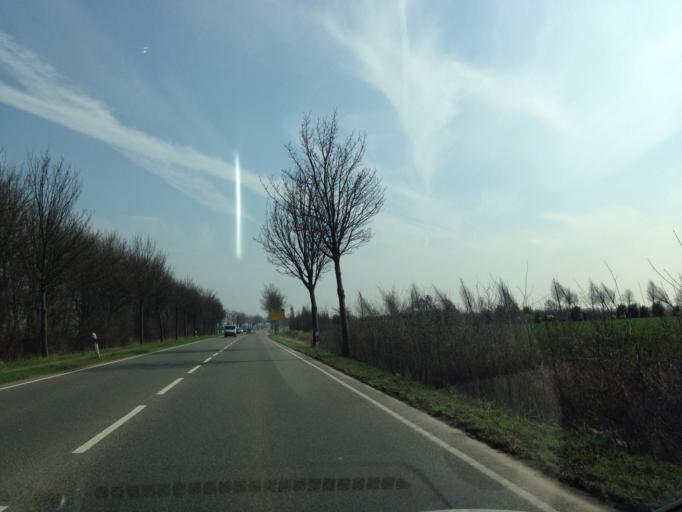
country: DE
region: North Rhine-Westphalia
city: Huckelhoven
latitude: 51.0924
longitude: 6.2582
